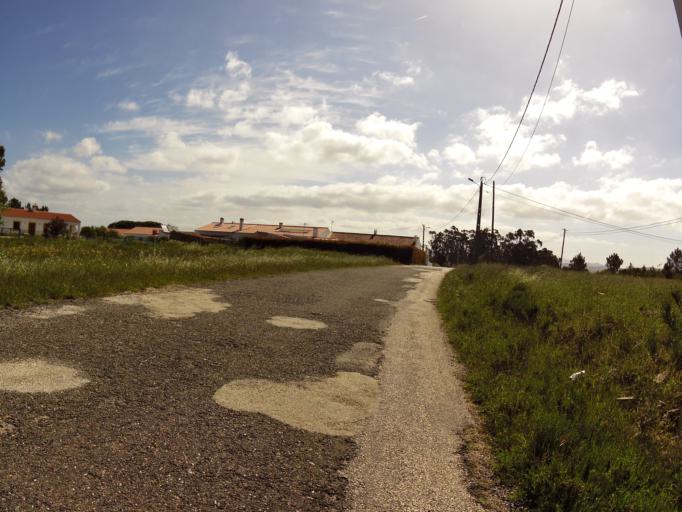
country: PT
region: Faro
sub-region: Aljezur
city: Aljezur
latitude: 37.3409
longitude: -8.8025
